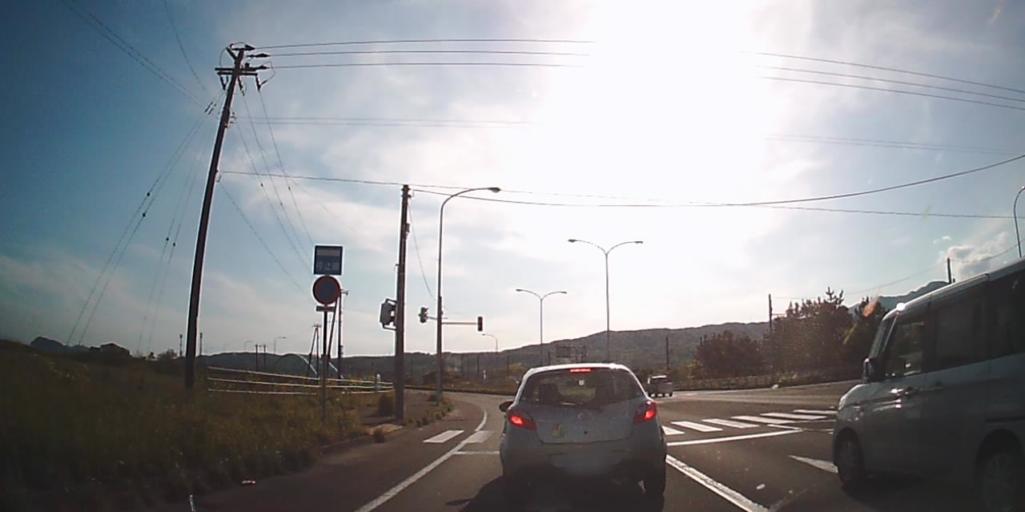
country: JP
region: Hokkaido
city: Muroran
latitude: 42.4047
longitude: 141.1024
